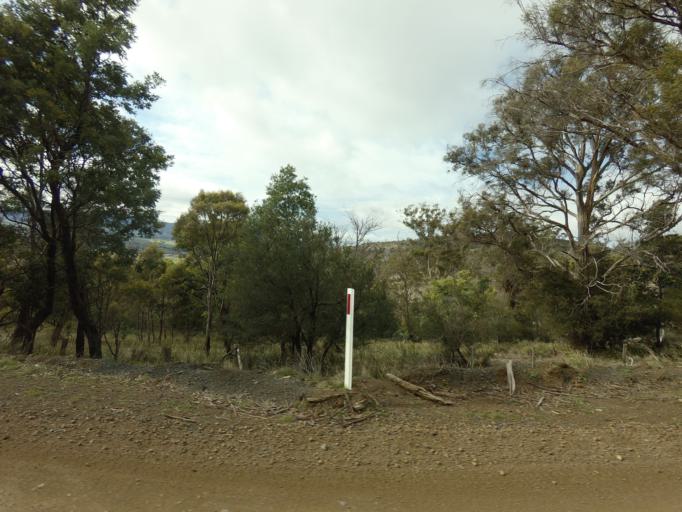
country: AU
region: Tasmania
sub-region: Derwent Valley
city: New Norfolk
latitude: -42.7281
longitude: 146.8665
